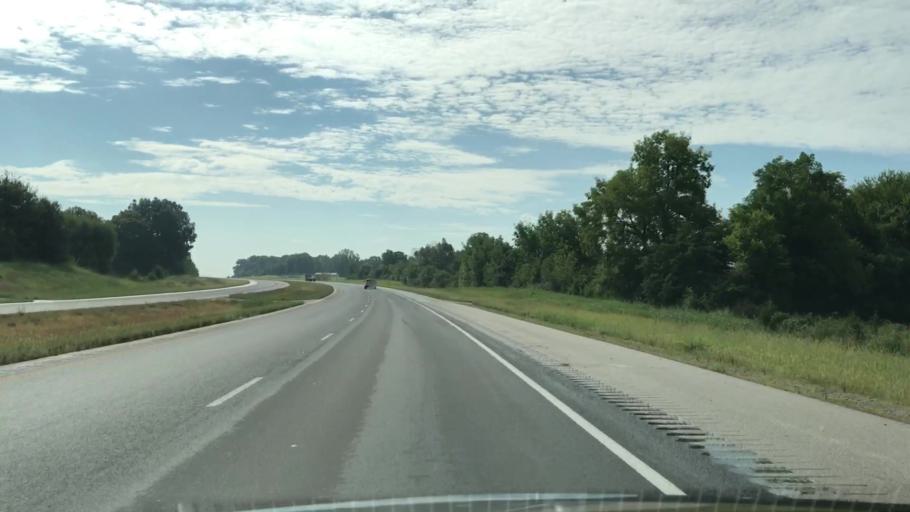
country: US
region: Kentucky
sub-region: Warren County
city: Plano
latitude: 36.8650
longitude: -86.3508
